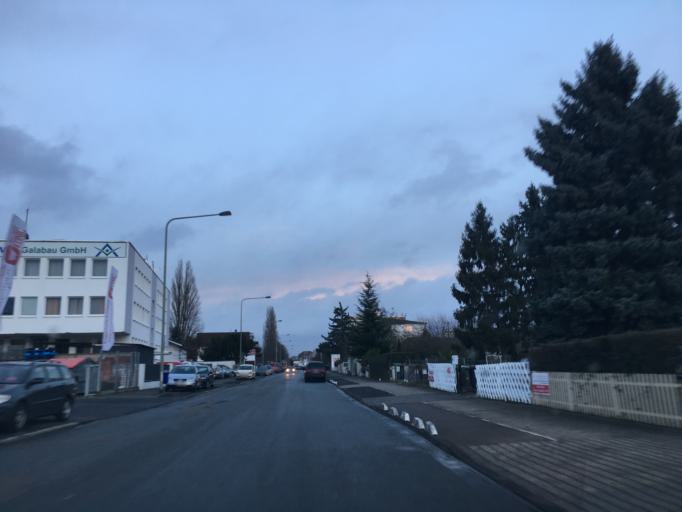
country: DE
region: Hesse
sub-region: Regierungsbezirk Darmstadt
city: Offenbach
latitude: 50.1284
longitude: 8.7478
